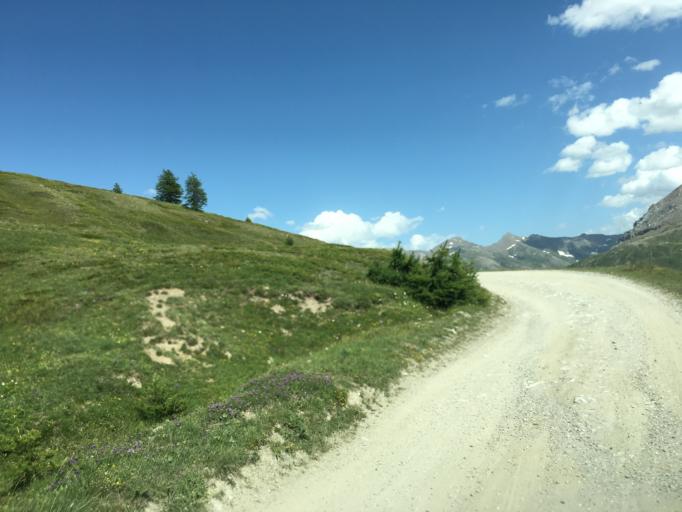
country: IT
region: Piedmont
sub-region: Provincia di Torino
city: Sestriere
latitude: 44.9784
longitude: 6.8739
